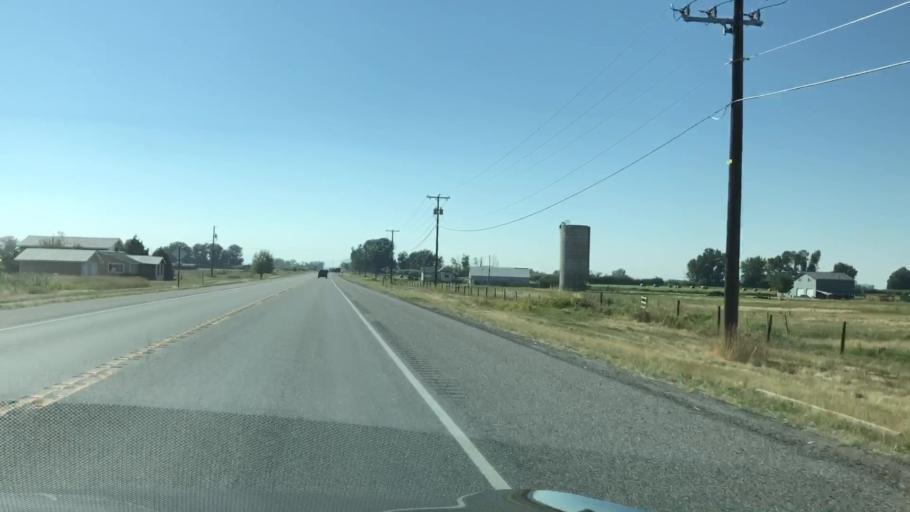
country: US
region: Montana
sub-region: Gallatin County
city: Belgrade
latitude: 45.7293
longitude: -111.1452
